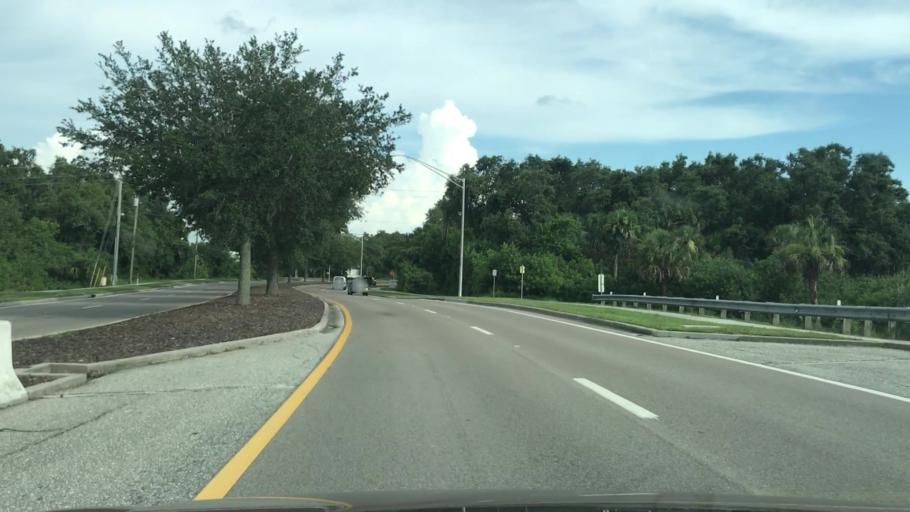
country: US
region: Florida
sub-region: Sarasota County
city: Venice Gardens
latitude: 27.0581
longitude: -82.3954
